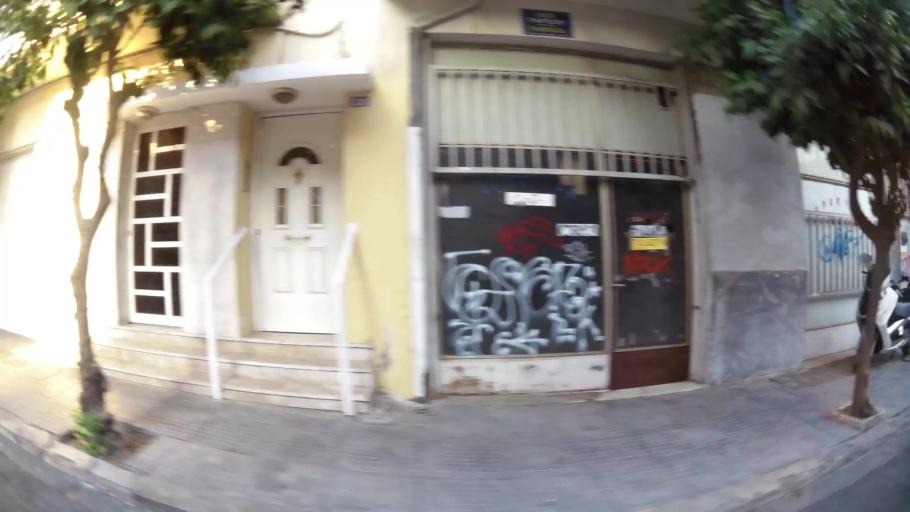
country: GR
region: Attica
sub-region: Nomos Piraios
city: Nikaia
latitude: 37.9658
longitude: 23.6391
